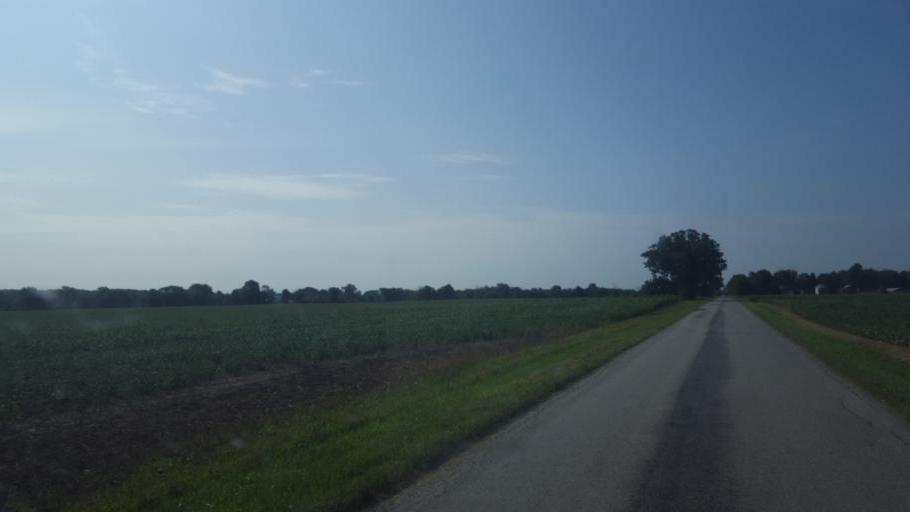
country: US
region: Ohio
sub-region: Morrow County
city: Cardington
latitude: 40.5538
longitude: -82.9194
